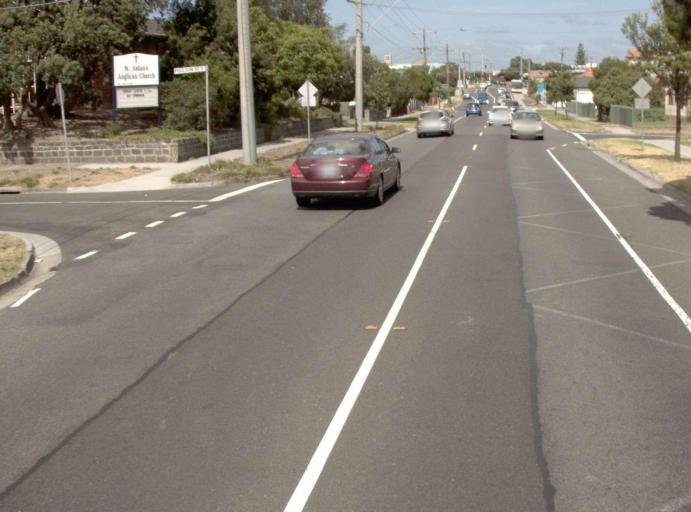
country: AU
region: Victoria
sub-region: Kingston
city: Bonbeach
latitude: -38.0752
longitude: 145.1262
